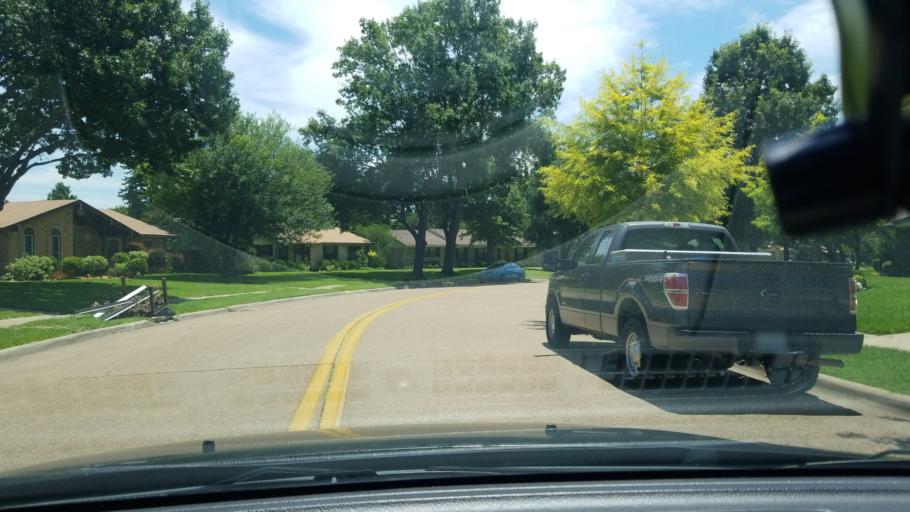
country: US
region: Texas
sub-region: Dallas County
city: Mesquite
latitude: 32.7958
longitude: -96.6482
